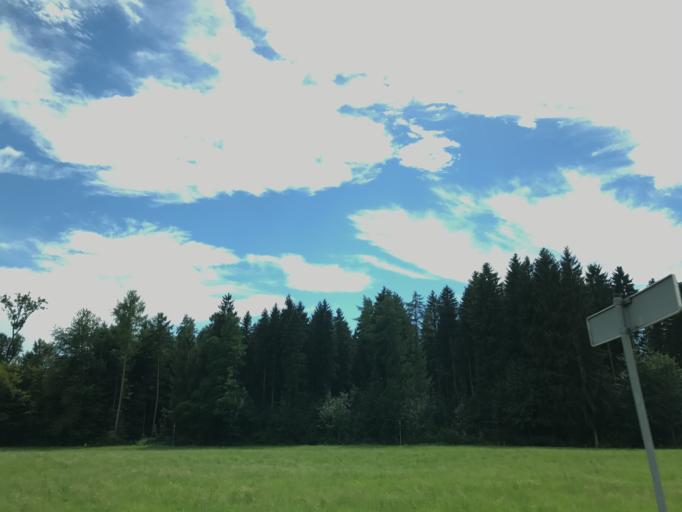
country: DE
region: Baden-Wuerttemberg
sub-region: Tuebingen Region
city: Wangen im Allgau
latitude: 47.7038
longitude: 9.8209
